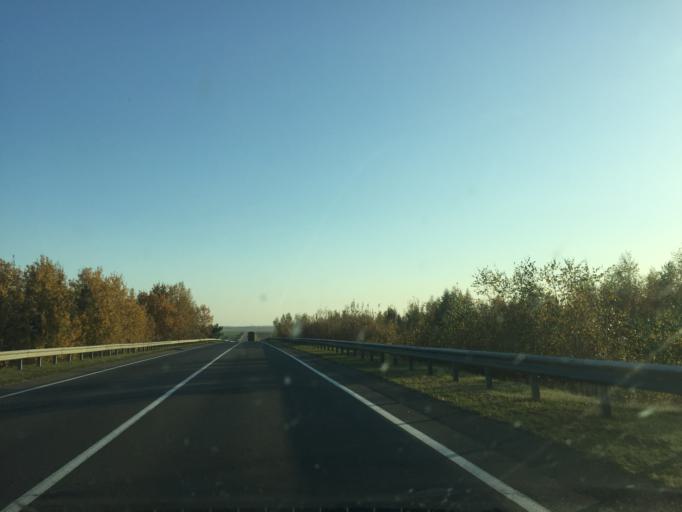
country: BY
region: Mogilev
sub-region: Mahilyowski Rayon
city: Kadino
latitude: 53.8579
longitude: 30.4799
